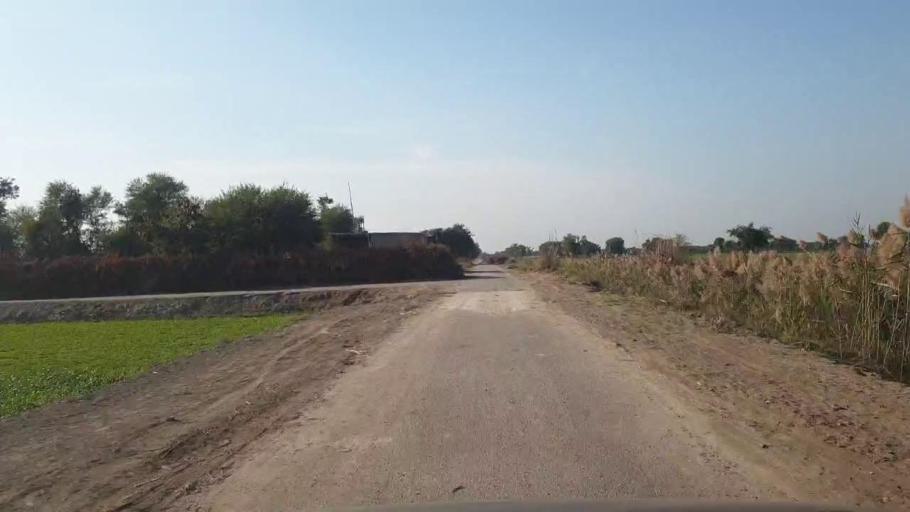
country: PK
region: Sindh
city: Shahpur Chakar
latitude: 26.1726
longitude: 68.6526
